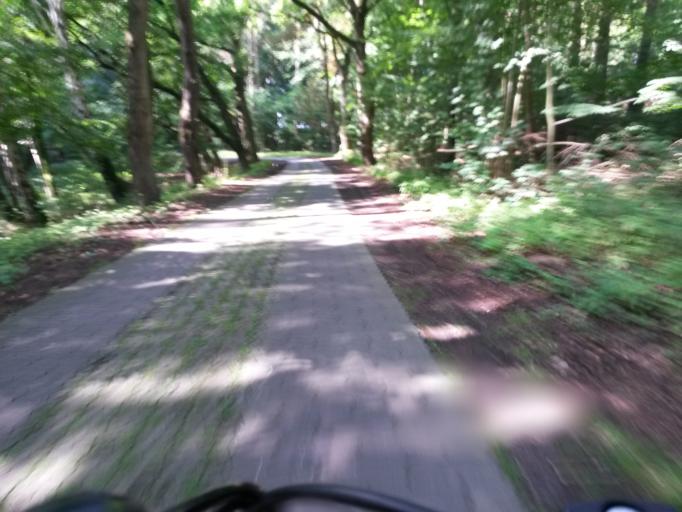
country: DE
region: Brandenburg
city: Althuttendorf
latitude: 53.0239
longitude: 13.8695
